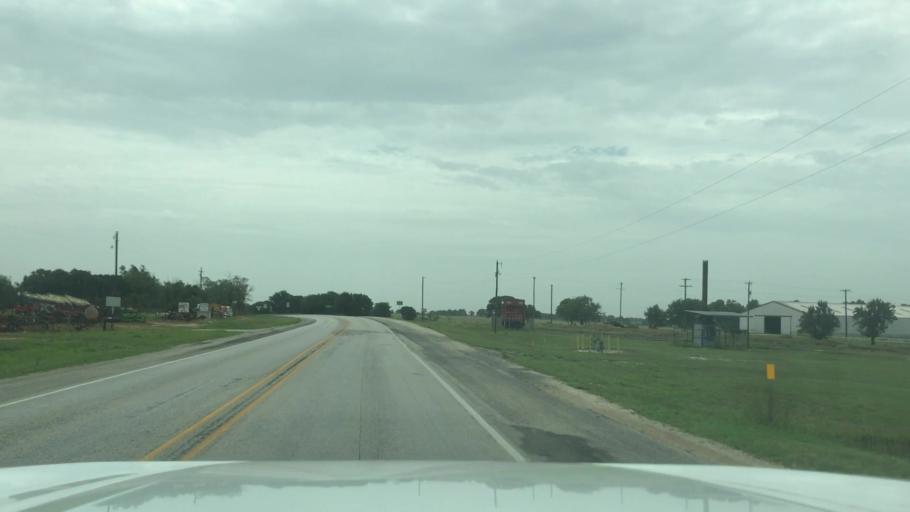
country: US
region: Texas
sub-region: Eastland County
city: Gorman
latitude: 32.2064
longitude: -98.6620
